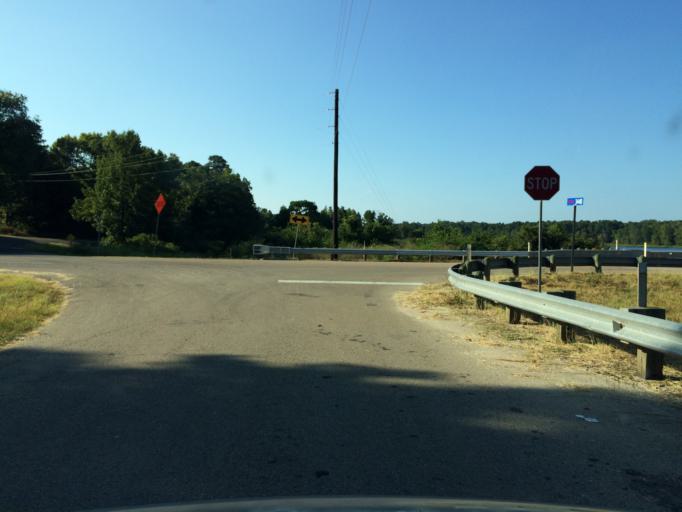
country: US
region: Texas
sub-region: Wood County
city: Hawkins
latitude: 32.6358
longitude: -95.2622
